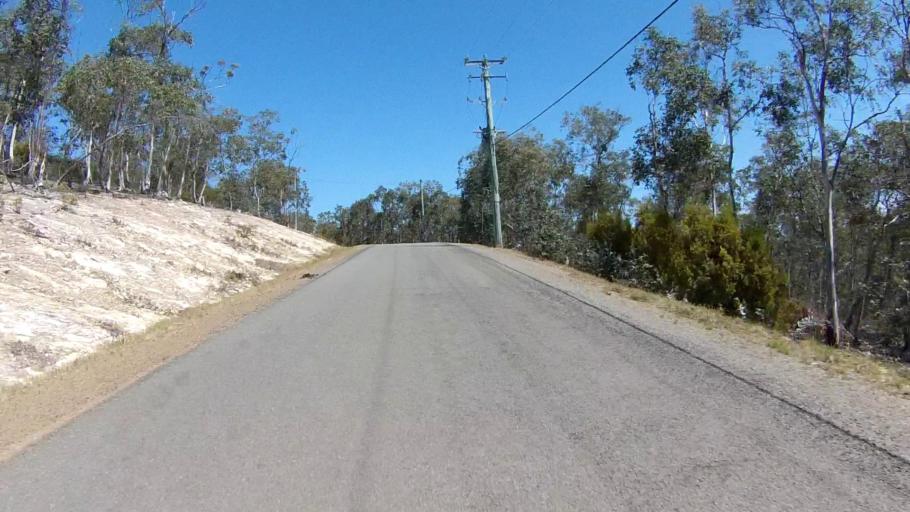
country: AU
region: Tasmania
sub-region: Clarence
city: Sandford
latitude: -42.9596
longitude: 147.4826
